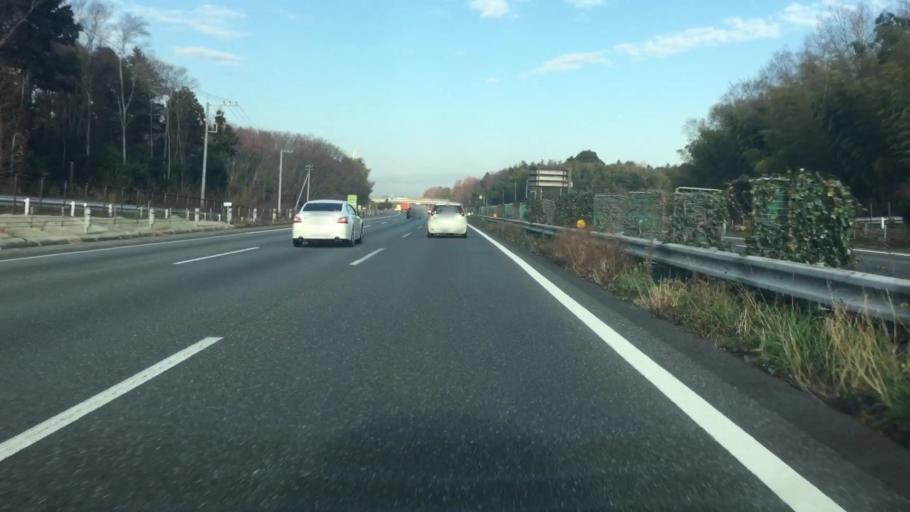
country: JP
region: Saitama
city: Ogawa
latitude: 36.1065
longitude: 139.2762
